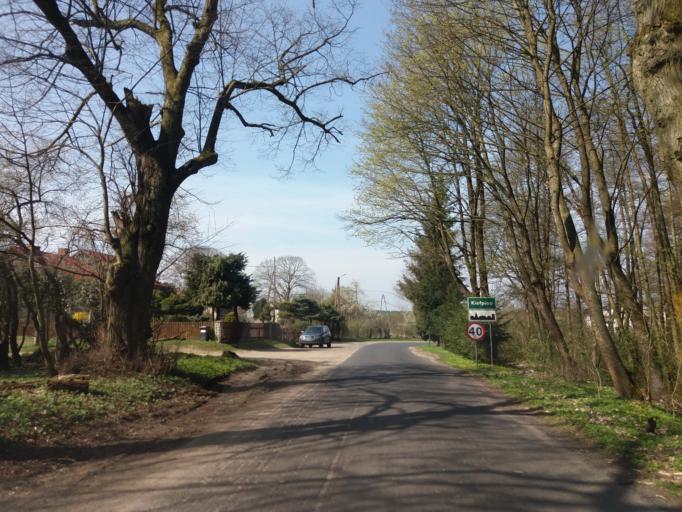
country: PL
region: West Pomeranian Voivodeship
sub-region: Powiat choszczenski
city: Drawno
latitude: 53.1867
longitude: 15.6463
